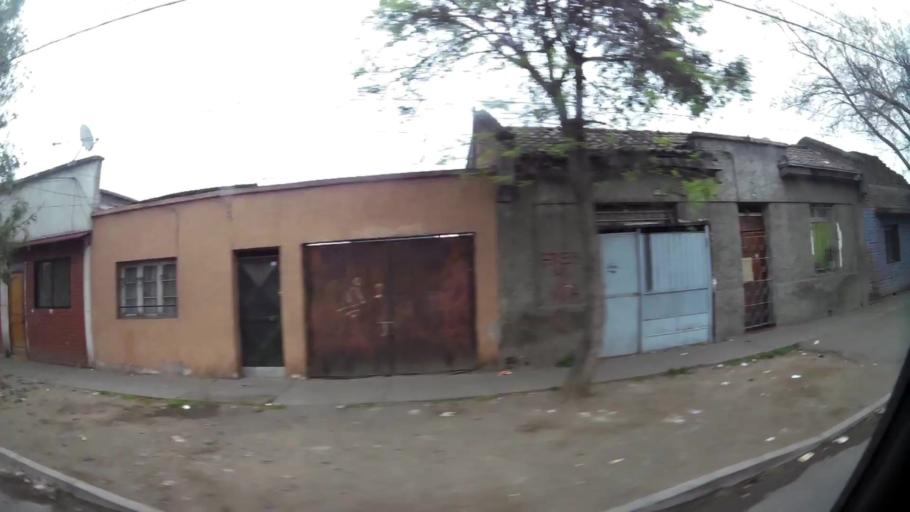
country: CL
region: Santiago Metropolitan
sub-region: Provincia de Santiago
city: Santiago
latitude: -33.4892
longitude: -70.6356
